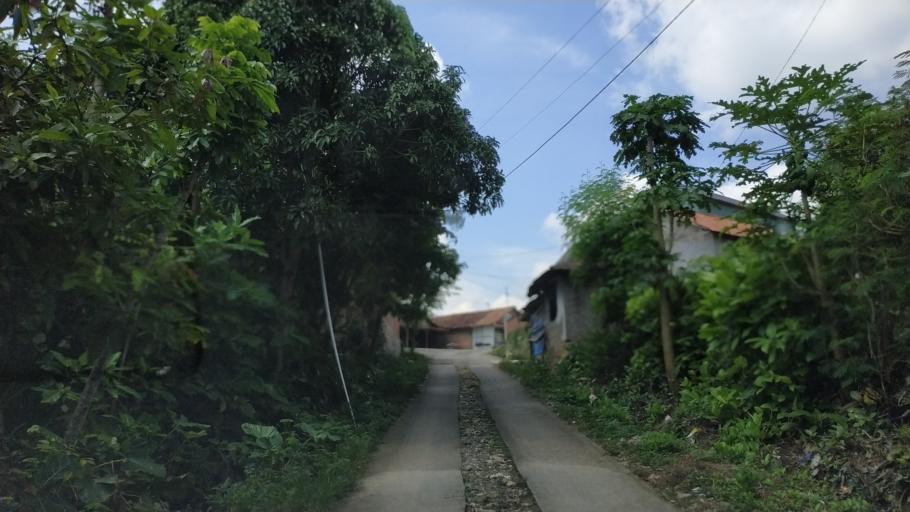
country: ID
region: Central Java
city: Guyangan
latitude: -7.0054
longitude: 111.1082
